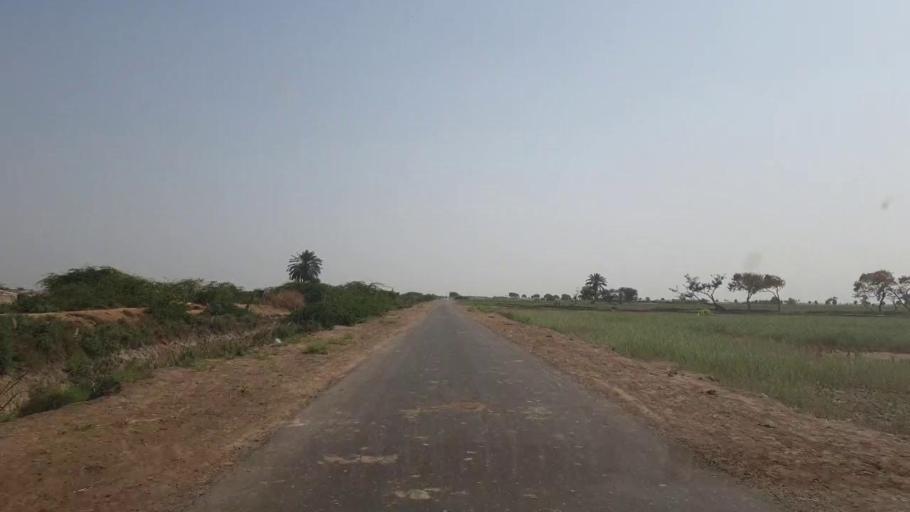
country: PK
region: Sindh
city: Jati
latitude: 24.4559
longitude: 68.5135
